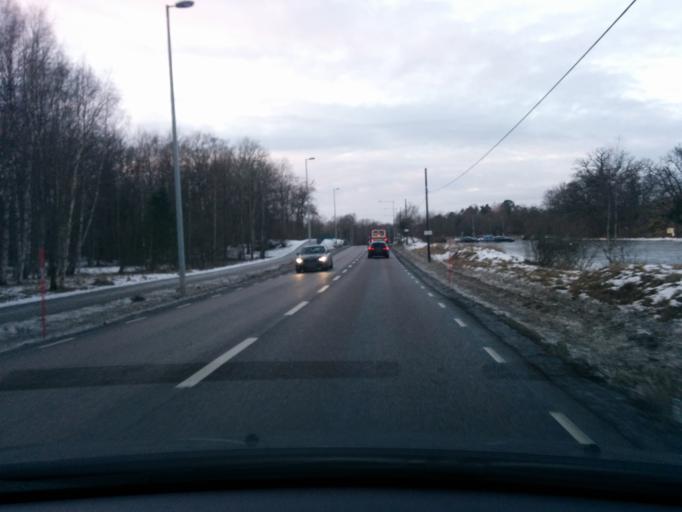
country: SE
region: Stockholm
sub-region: Nacka Kommun
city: Nacka
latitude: 59.2882
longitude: 18.1647
